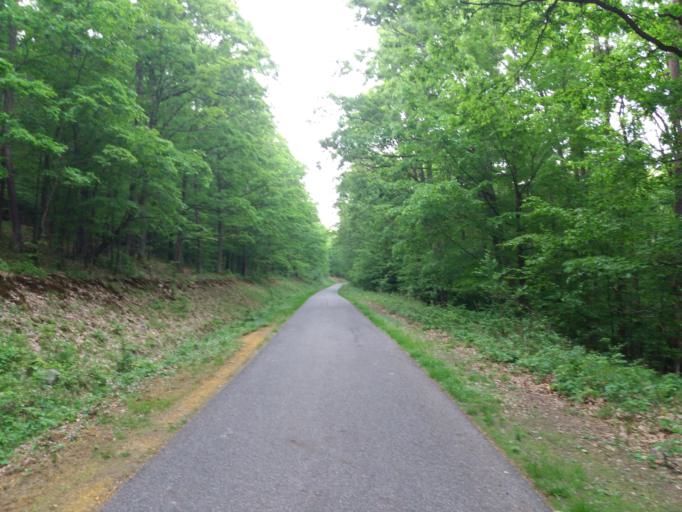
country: HU
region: Borsod-Abauj-Zemplen
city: Gonc
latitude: 48.4986
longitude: 21.3906
